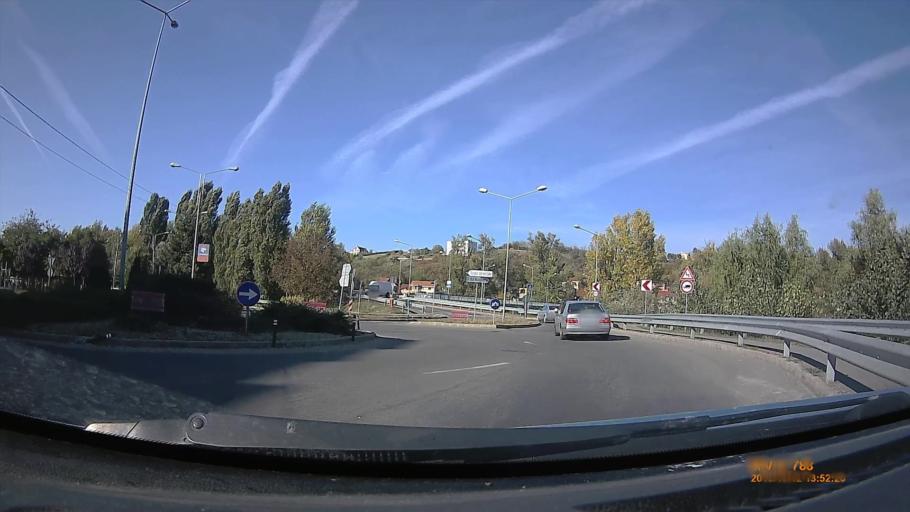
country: RO
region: Bihor
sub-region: Comuna Biharea
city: Oradea
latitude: 47.0503
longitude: 21.9609
